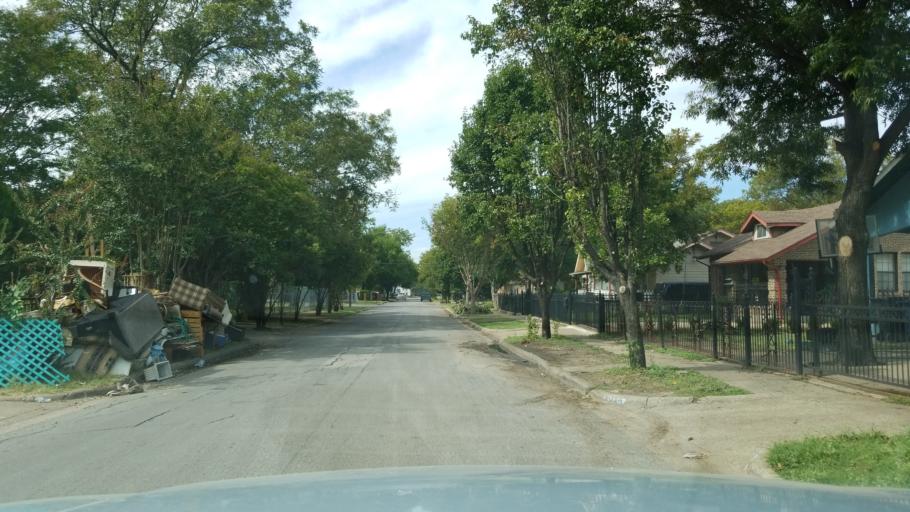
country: US
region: Texas
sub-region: Dallas County
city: Dallas
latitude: 32.7864
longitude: -96.7423
